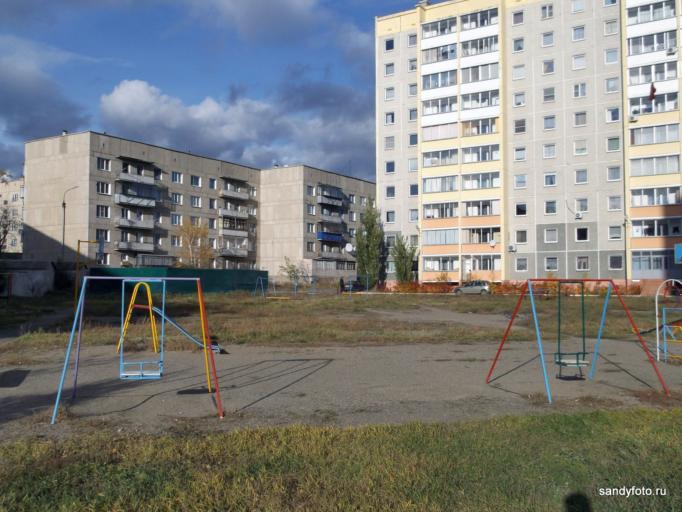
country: RU
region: Chelyabinsk
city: Troitsk
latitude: 54.0774
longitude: 61.5272
